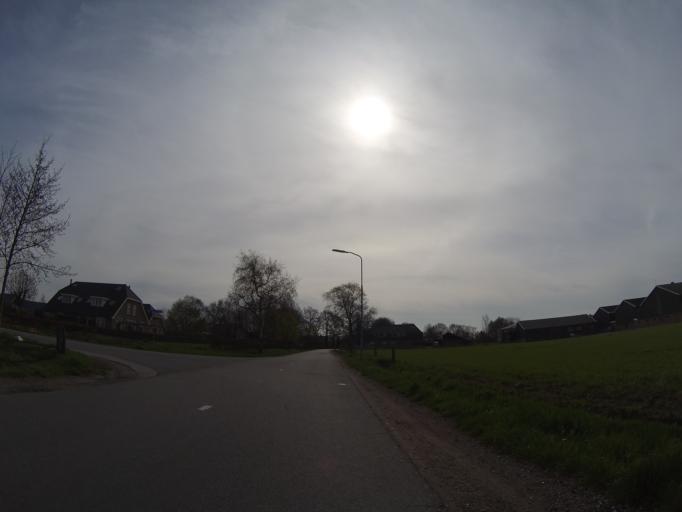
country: NL
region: Gelderland
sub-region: Gemeente Barneveld
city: Voorthuizen
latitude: 52.1853
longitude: 5.5799
